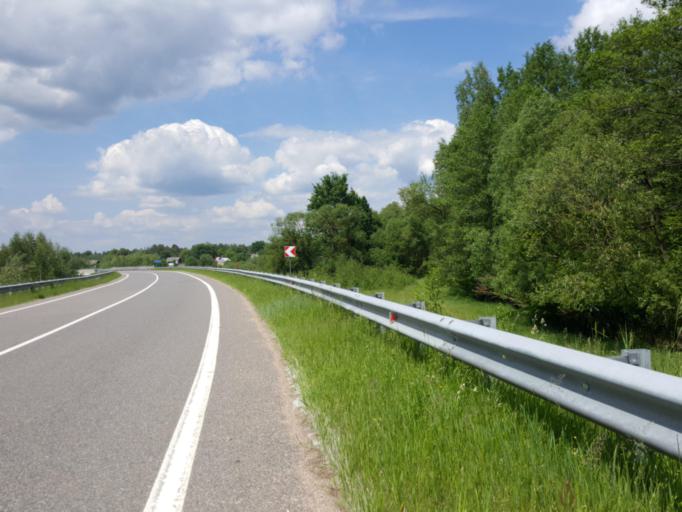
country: BY
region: Brest
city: Kamyanyuki
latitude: 52.5466
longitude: 23.6528
